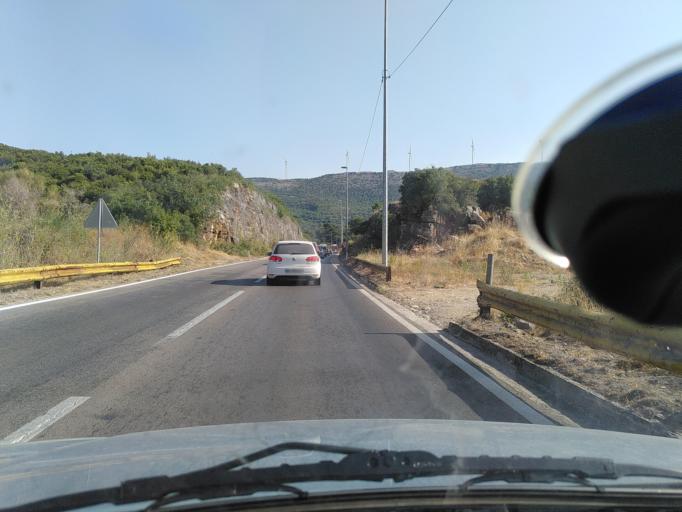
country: ME
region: Ulcinj
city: Ulcinj
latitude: 41.9591
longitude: 19.1909
